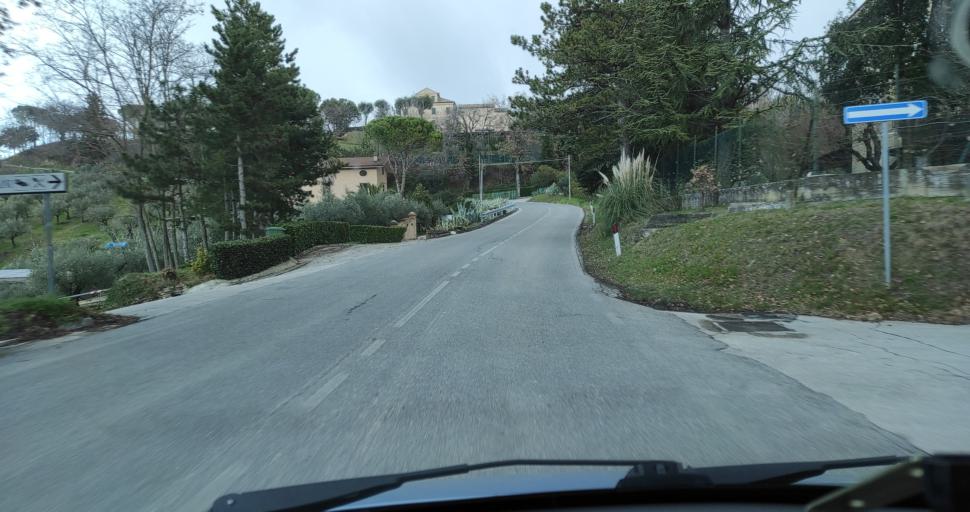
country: IT
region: The Marches
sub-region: Provincia di Macerata
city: Mogliano
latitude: 43.1923
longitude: 13.4685
